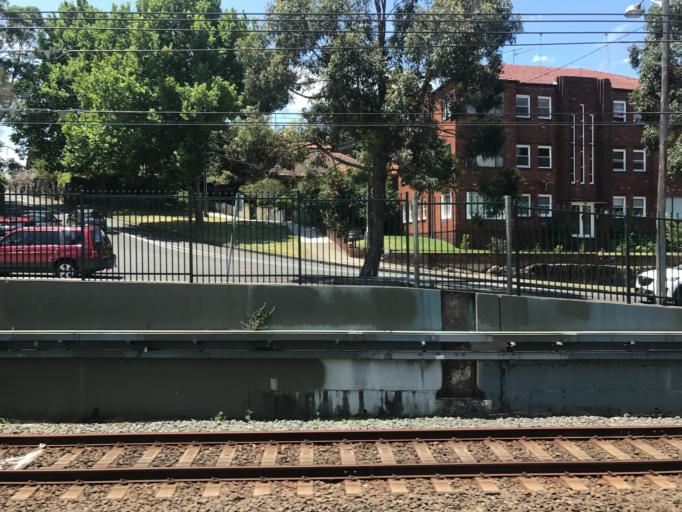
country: AU
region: New South Wales
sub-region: North Sydney
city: North Sydney
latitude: -33.8396
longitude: 151.1996
